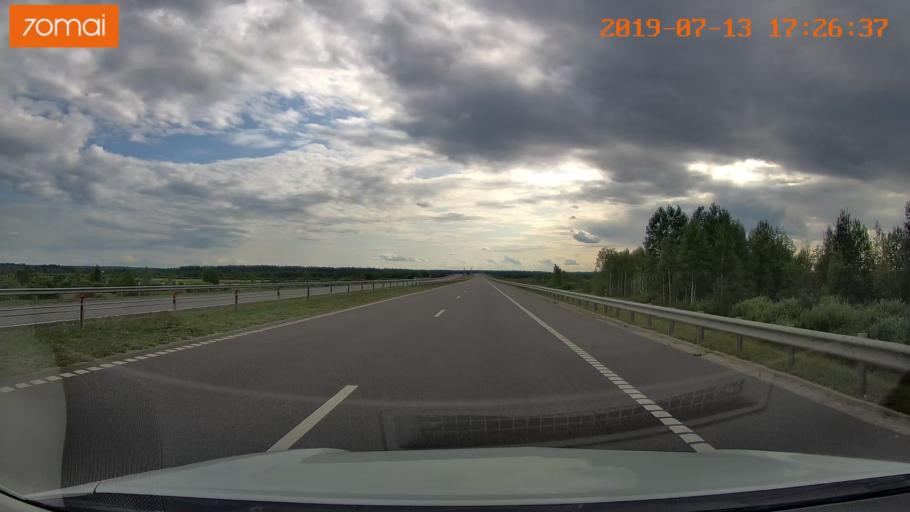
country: BY
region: Mogilev
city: Babruysk
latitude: 53.2503
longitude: 29.1781
